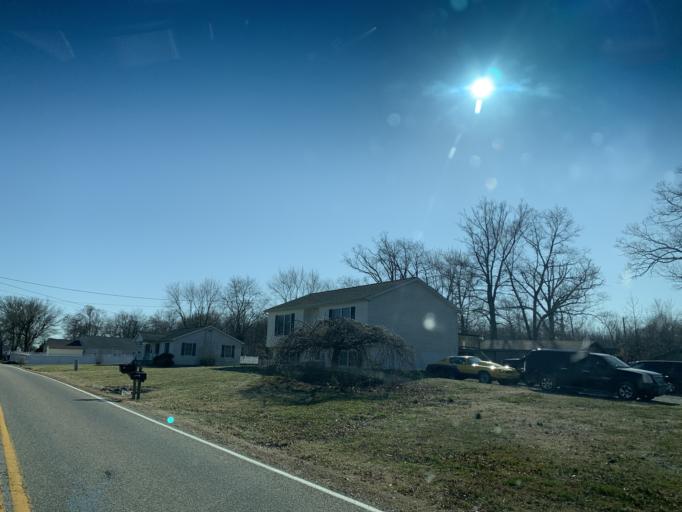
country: US
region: Maryland
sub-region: Cecil County
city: North East
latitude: 39.6730
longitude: -75.9036
